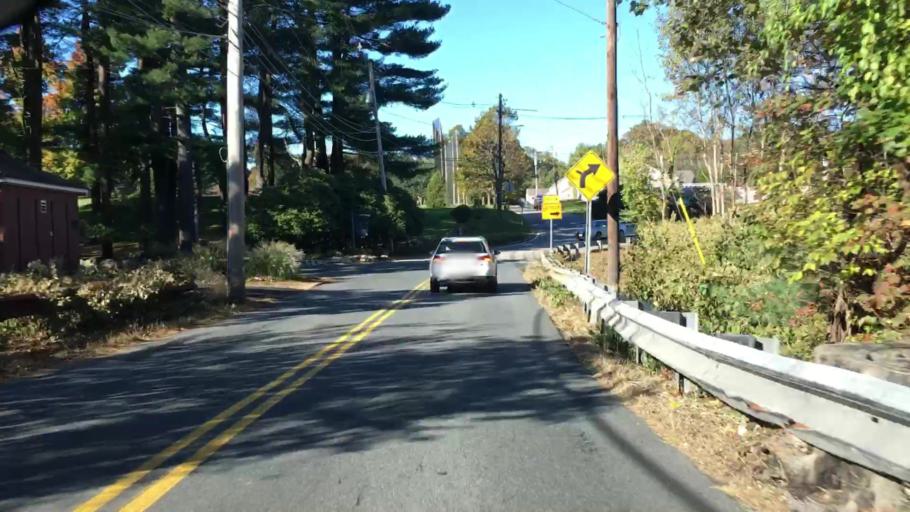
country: US
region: Massachusetts
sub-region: Middlesex County
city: Framingham Center
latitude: 42.2927
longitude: -71.4664
